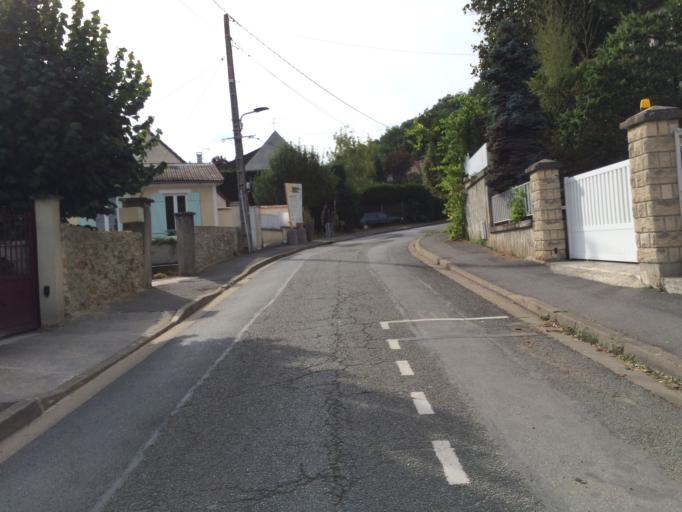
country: FR
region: Ile-de-France
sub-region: Departement de l'Essonne
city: Orsay
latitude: 48.7069
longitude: 2.2100
